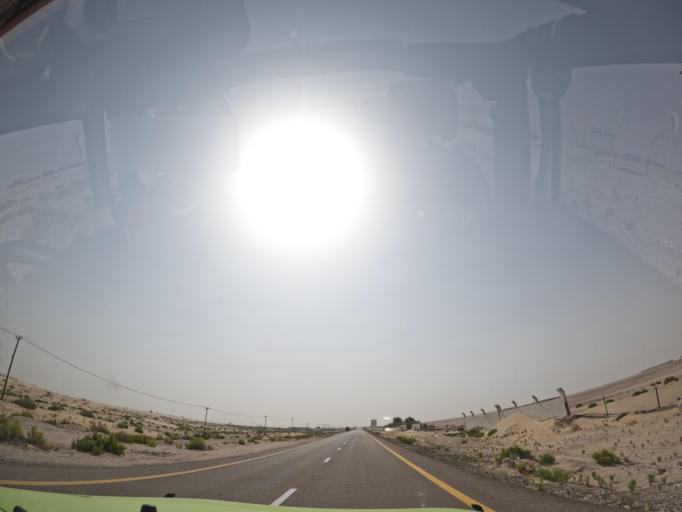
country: AE
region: Dubai
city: Dubai
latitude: 24.6680
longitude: 55.1727
